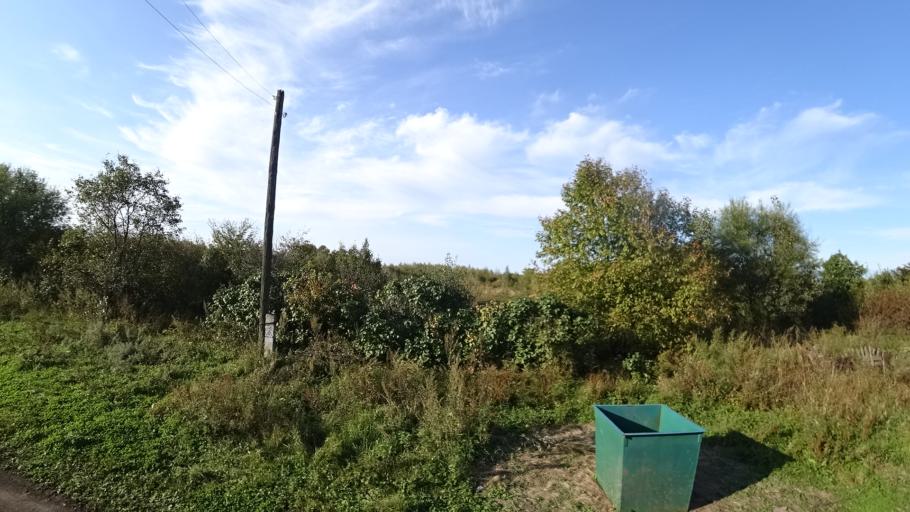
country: RU
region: Amur
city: Arkhara
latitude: 49.3497
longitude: 130.1182
